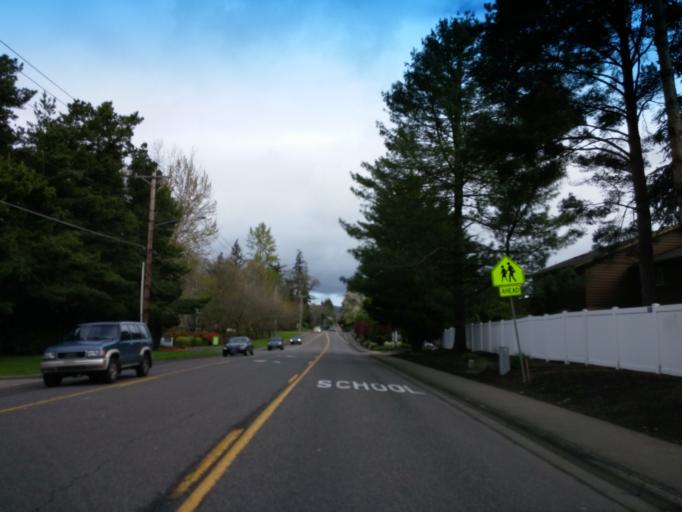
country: US
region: Oregon
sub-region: Washington County
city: Cedar Mill
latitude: 45.5325
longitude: -122.8244
